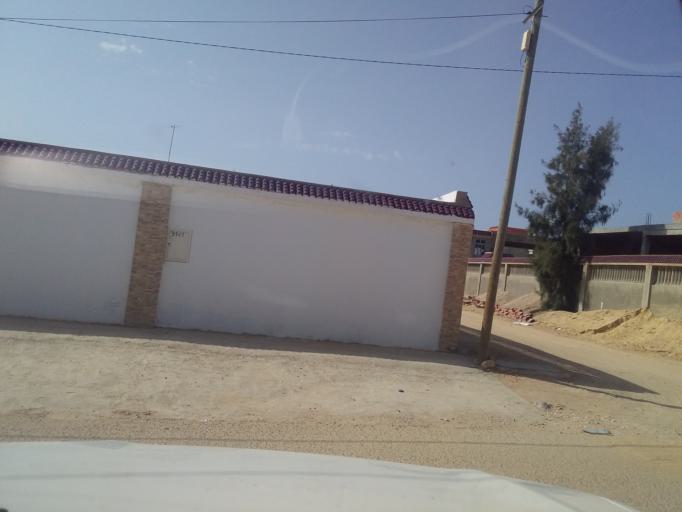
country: TN
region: Qabis
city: Gabes
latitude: 33.6330
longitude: 10.2852
